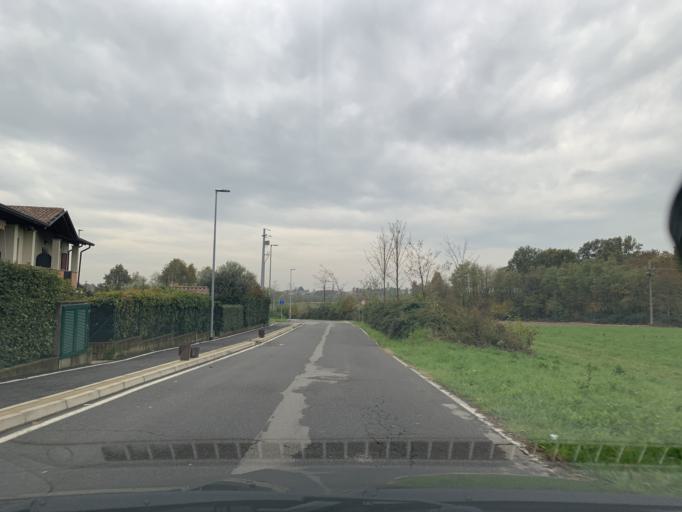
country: IT
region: Lombardy
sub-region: Provincia di Como
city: Puginate
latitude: 45.7124
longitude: 9.0545
